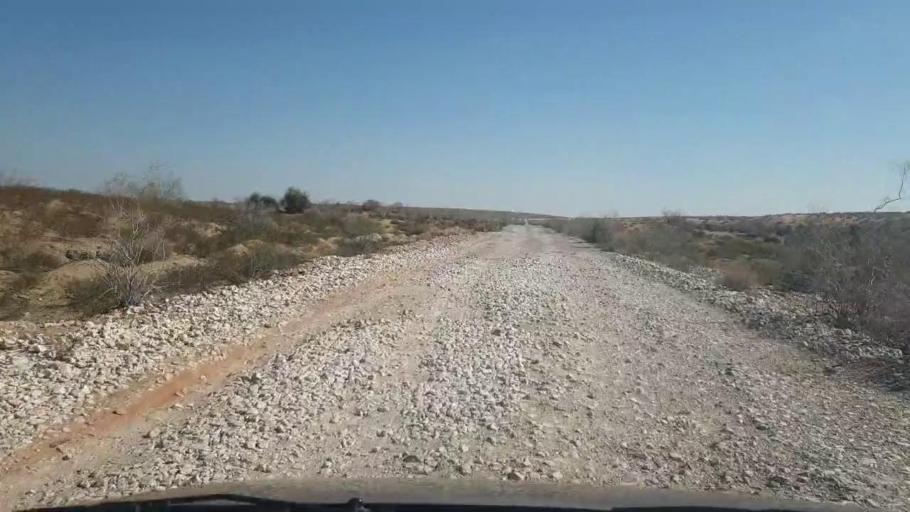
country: PK
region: Sindh
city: Bozdar
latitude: 27.0216
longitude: 68.7188
